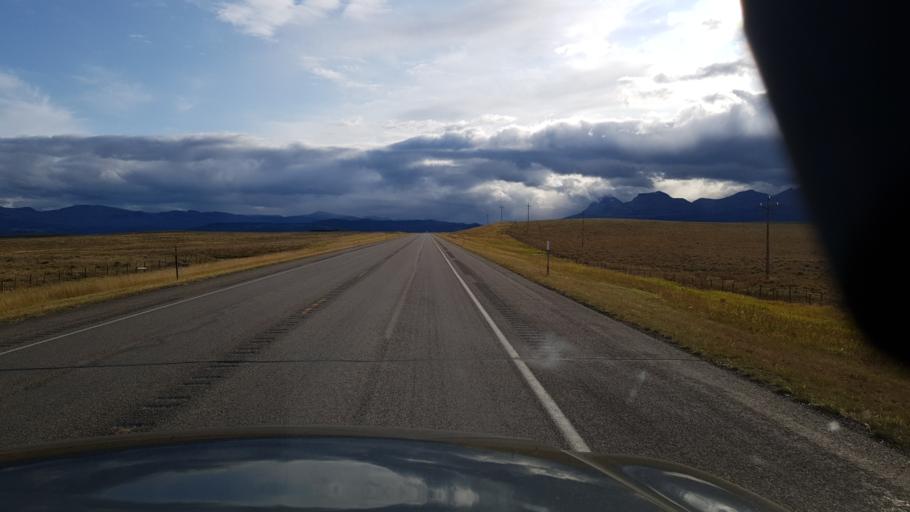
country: US
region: Montana
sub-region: Glacier County
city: South Browning
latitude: 48.4763
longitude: -113.1438
